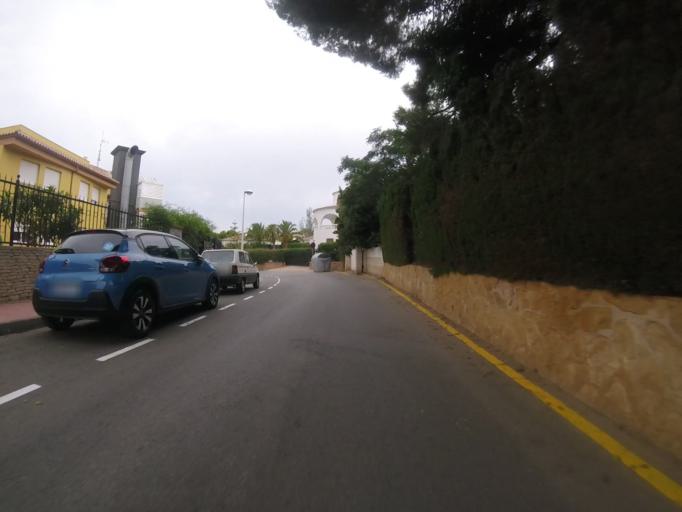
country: ES
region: Valencia
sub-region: Provincia de Castello
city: Alcoceber
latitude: 40.2581
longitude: 0.2892
